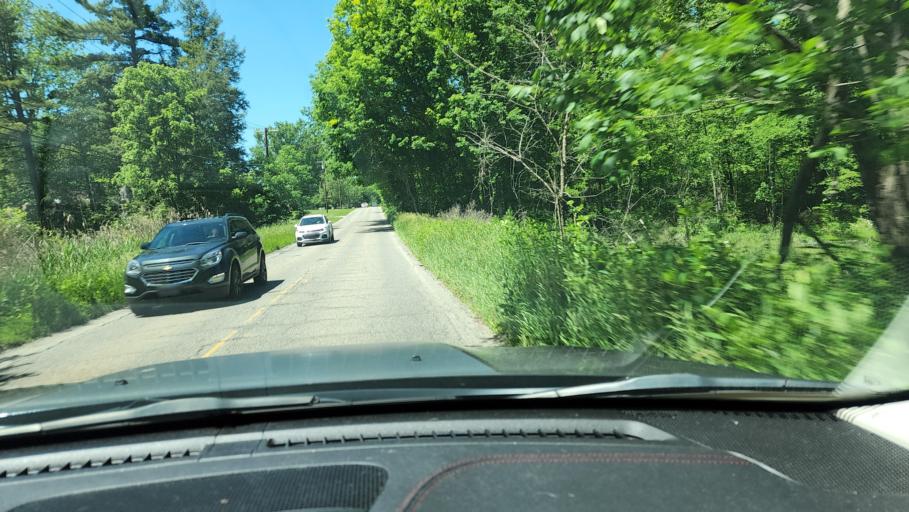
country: US
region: Ohio
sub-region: Trumbull County
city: Niles
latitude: 41.1641
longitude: -80.7785
